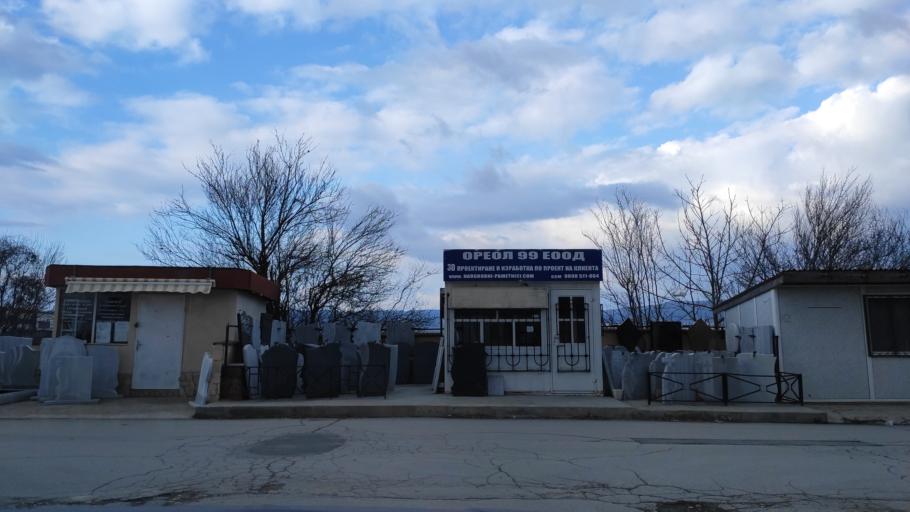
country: BG
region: Varna
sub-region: Obshtina Aksakovo
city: Aksakovo
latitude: 43.2243
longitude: 27.8061
